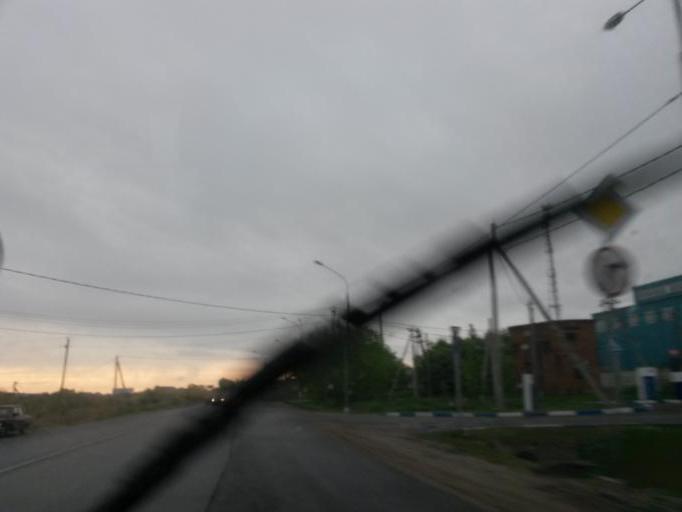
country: RU
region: Moskovskaya
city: Yam
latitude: 55.4850
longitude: 37.7562
